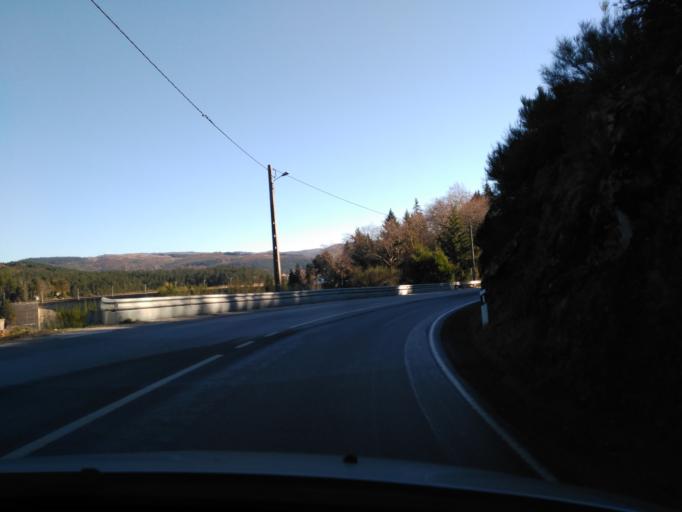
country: PT
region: Braga
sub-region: Vieira do Minho
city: Vieira do Minho
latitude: 41.6794
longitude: -7.9878
